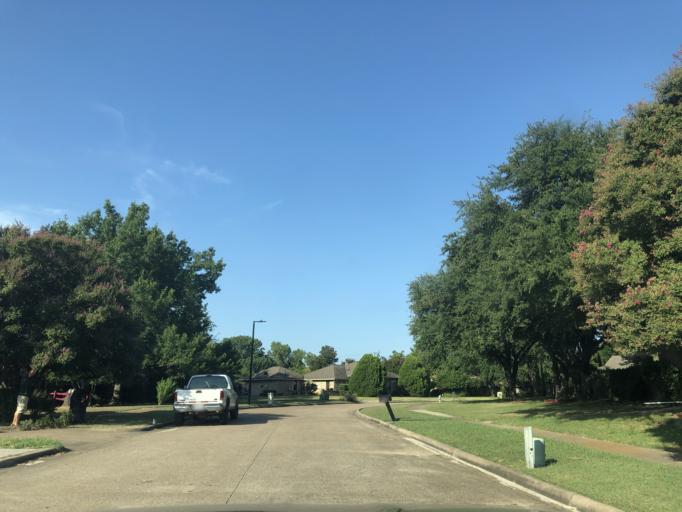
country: US
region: Texas
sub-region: Dallas County
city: Garland
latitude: 32.8678
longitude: -96.6363
